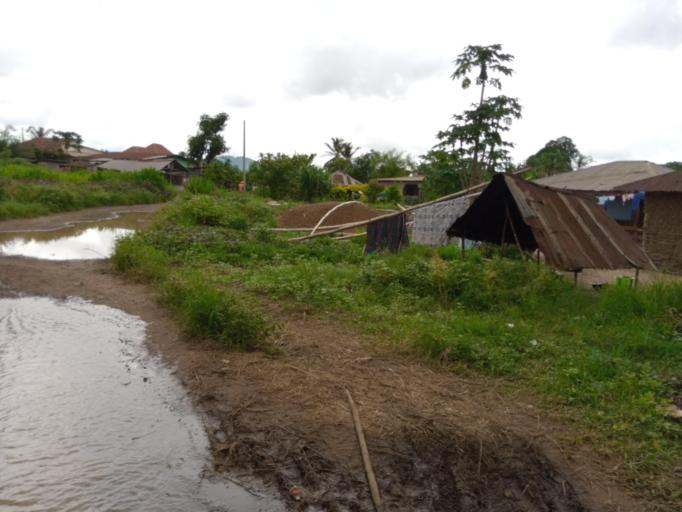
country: SL
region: Southern Province
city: Moyamba
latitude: 8.1658
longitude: -12.4253
